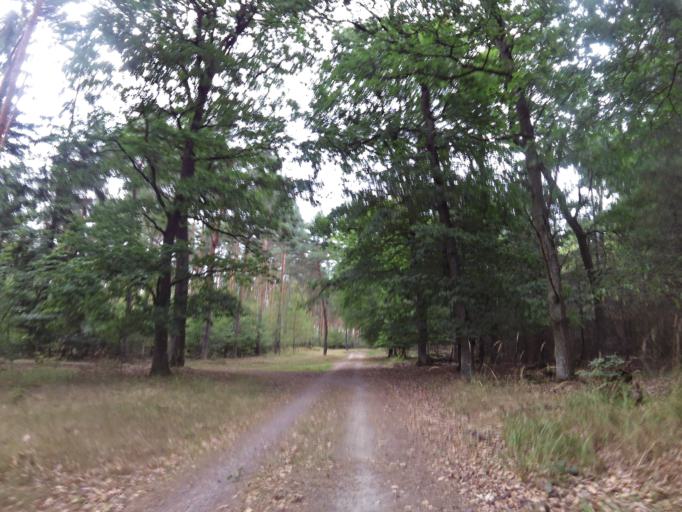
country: DE
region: Hesse
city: Morfelden-Walldorf
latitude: 50.0193
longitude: 8.5493
